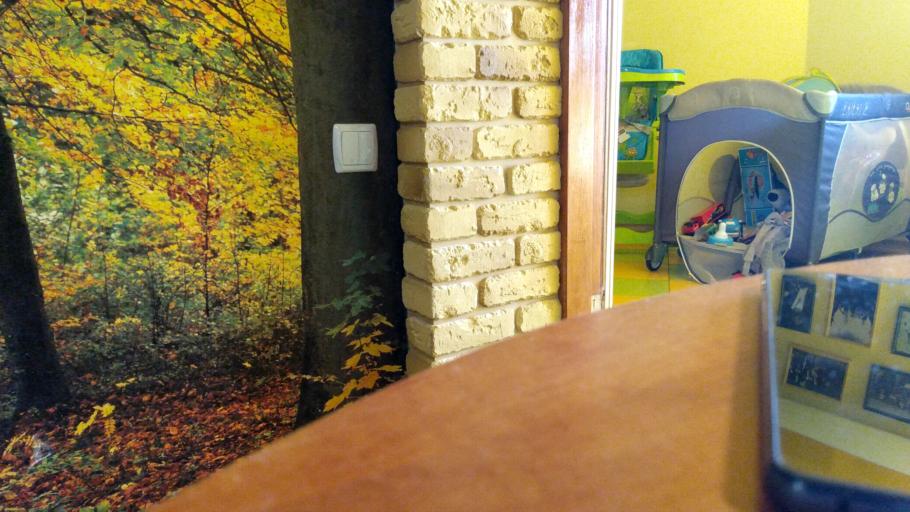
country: RU
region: Tverskaya
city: Kalashnikovo
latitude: 57.3876
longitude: 35.1801
